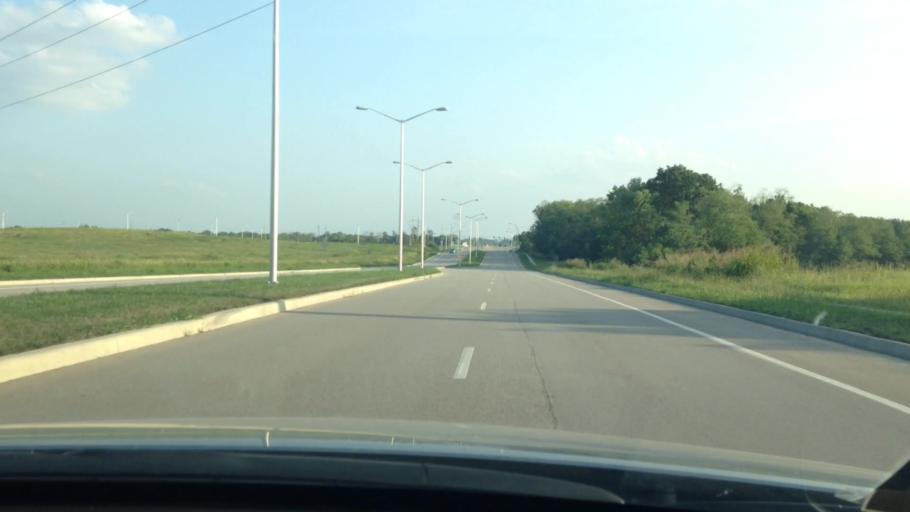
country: US
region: Missouri
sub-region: Platte County
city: Weatherby Lake
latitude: 39.2609
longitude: -94.6310
